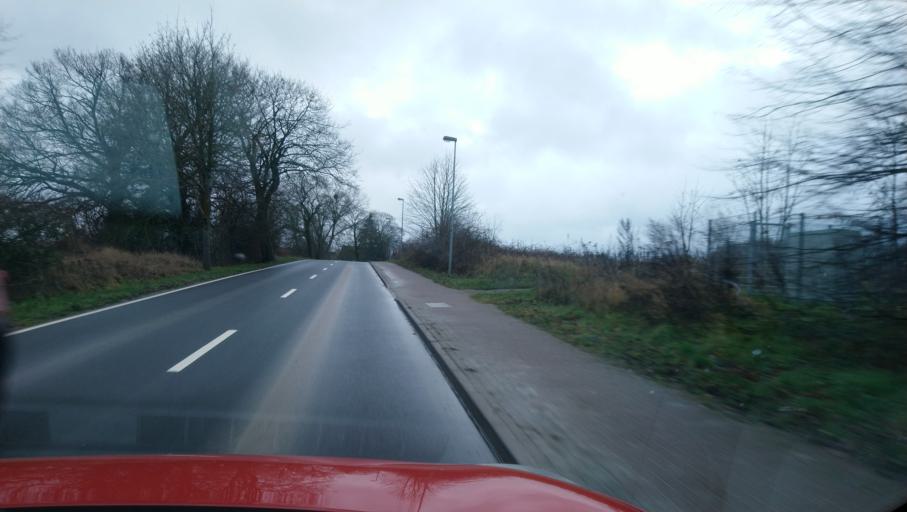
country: DE
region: Mecklenburg-Vorpommern
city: Seehof
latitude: 53.6792
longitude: 11.4282
